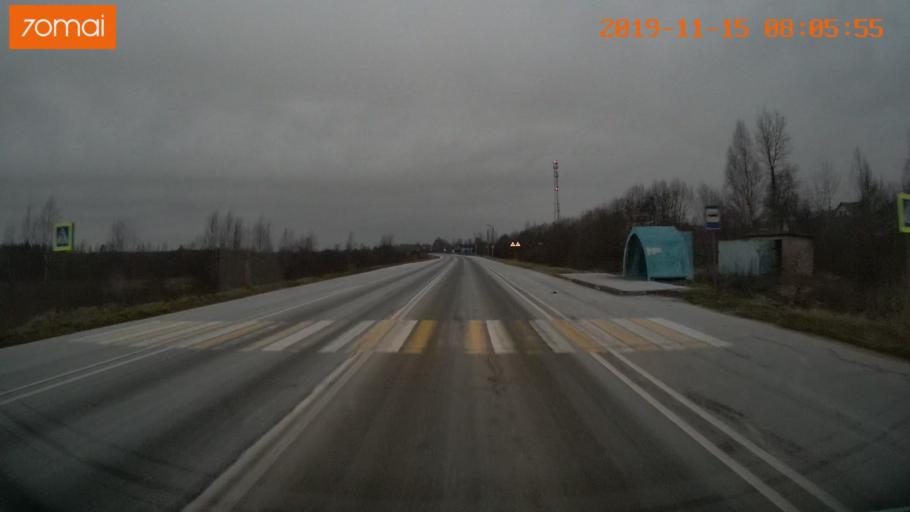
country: RU
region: Vologda
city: Cherepovets
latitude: 59.0195
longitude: 38.0482
